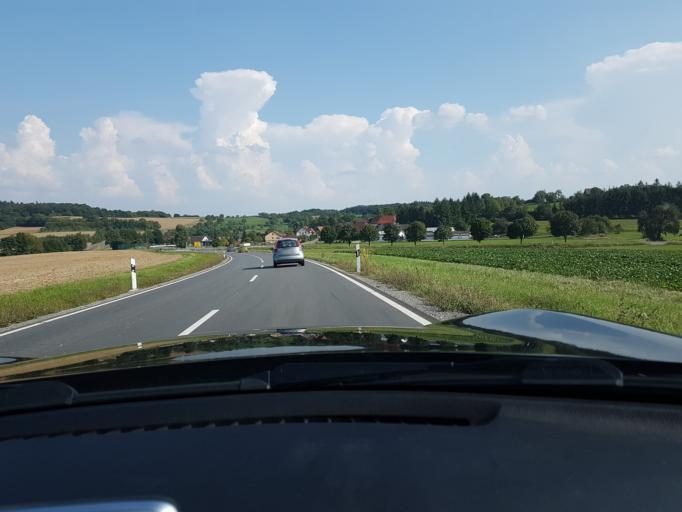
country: DE
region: Baden-Wuerttemberg
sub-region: Karlsruhe Region
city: Seckach
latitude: 49.4823
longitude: 9.3599
